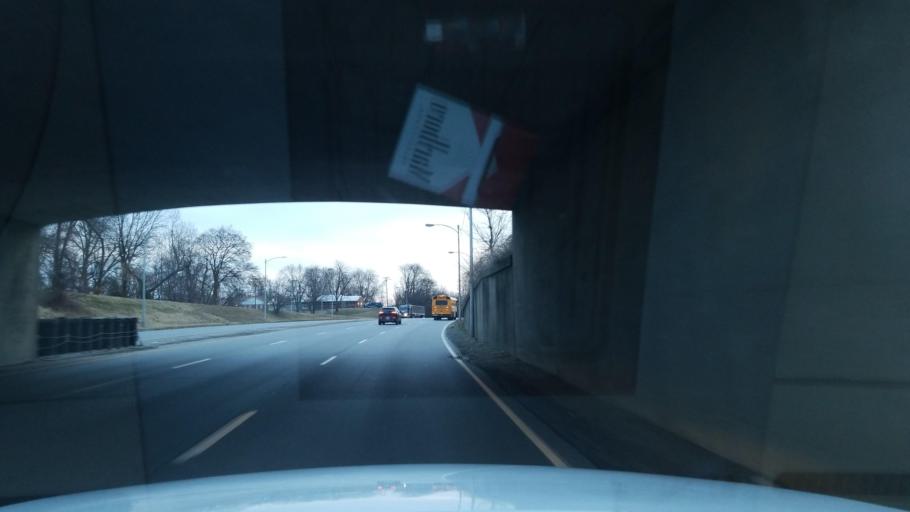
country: US
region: Indiana
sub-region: Vanderburgh County
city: Evansville
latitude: 37.9780
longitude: -87.6100
